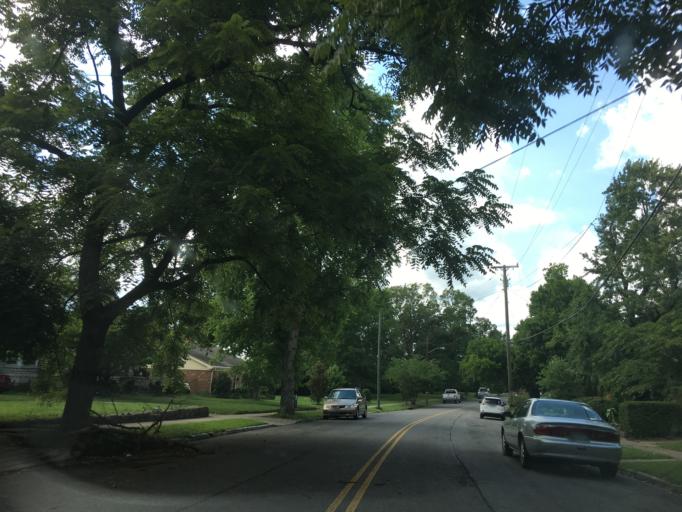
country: US
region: Tennessee
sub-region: Davidson County
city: Nashville
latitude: 36.1350
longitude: -86.8190
